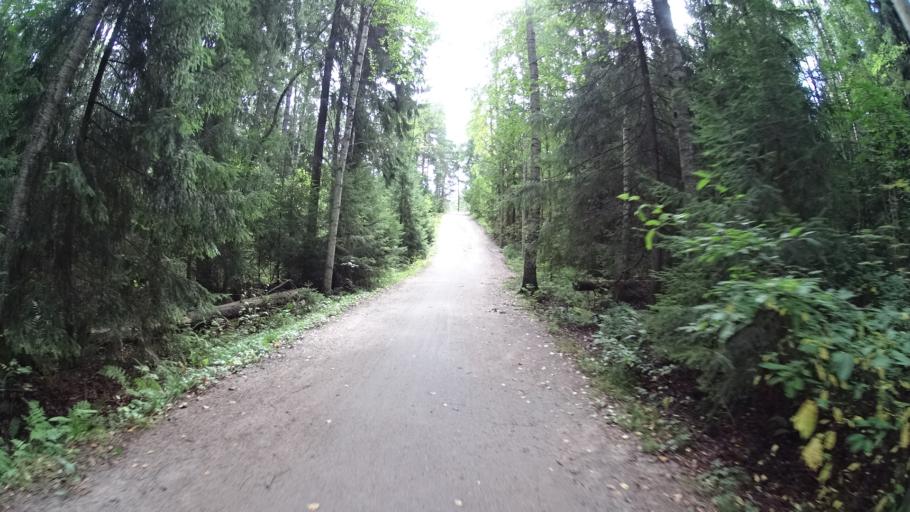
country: FI
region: Uusimaa
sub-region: Helsinki
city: Helsinki
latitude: 60.2600
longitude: 24.9037
